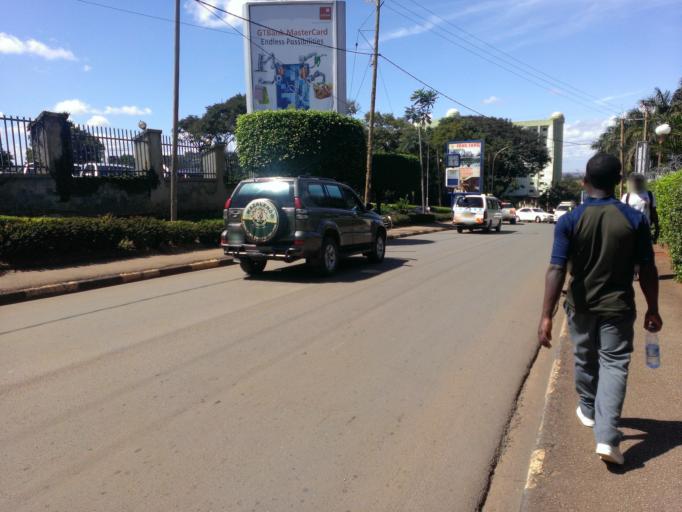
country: UG
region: Central Region
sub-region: Kampala District
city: Kampala
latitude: 0.3175
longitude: 32.5834
